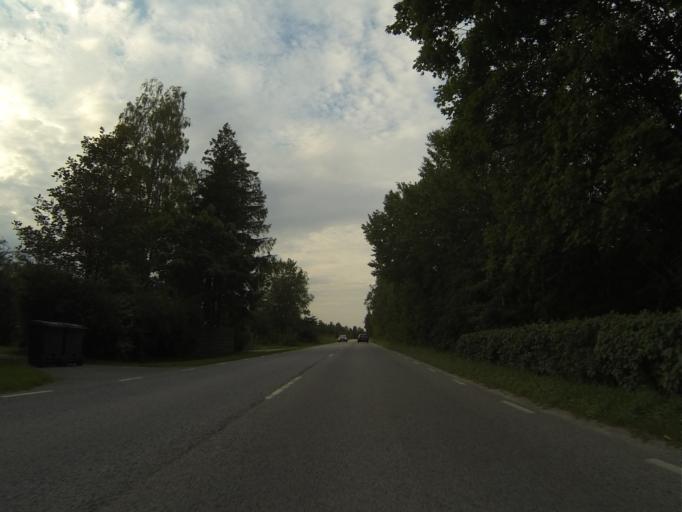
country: SE
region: Skane
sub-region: Lunds Kommun
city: Genarp
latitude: 55.6979
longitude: 13.3479
